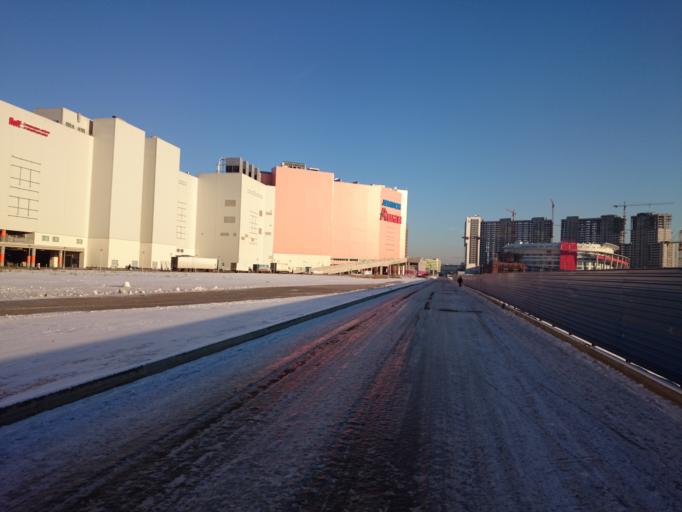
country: RU
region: Moscow
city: Sokol
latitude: 55.7890
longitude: 37.5294
